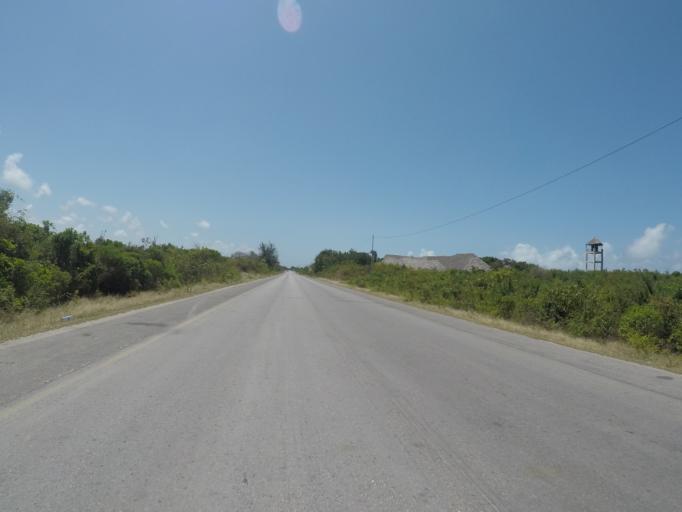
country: TZ
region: Zanzibar Central/South
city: Nganane
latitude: -6.2981
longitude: 39.5381
